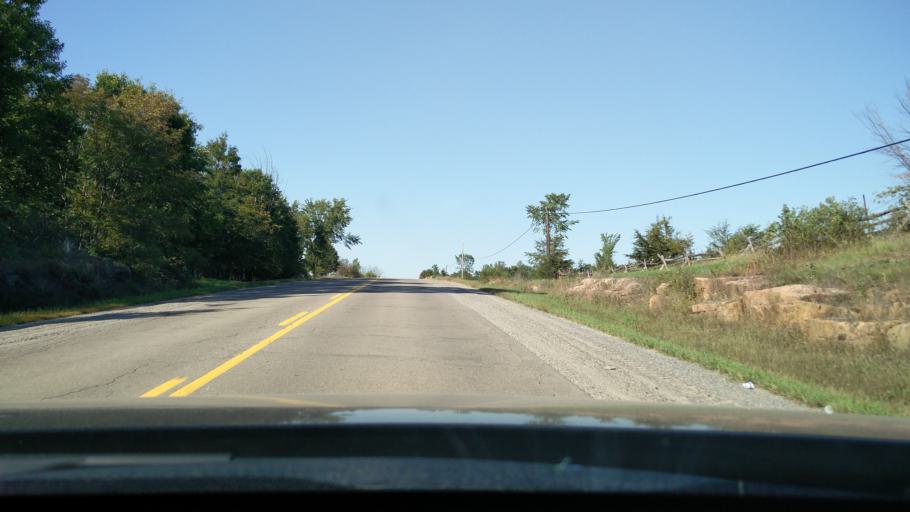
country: CA
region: Ontario
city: Perth
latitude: 44.7245
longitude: -76.3993
